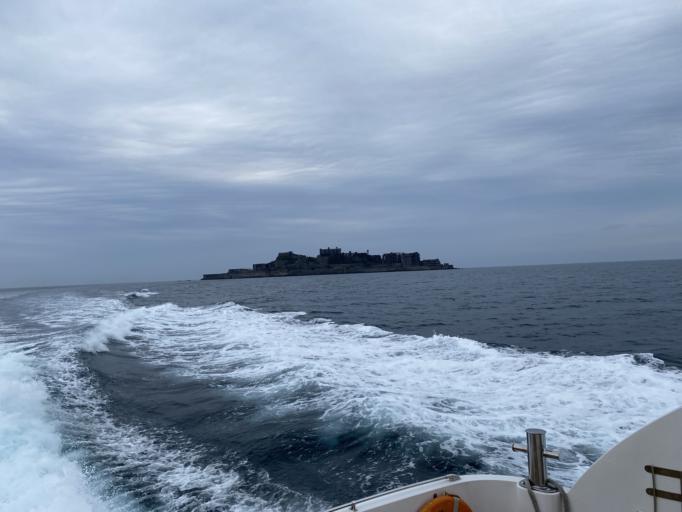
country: JP
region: Nagasaki
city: Nagasaki-shi
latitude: 32.6240
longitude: 129.7479
